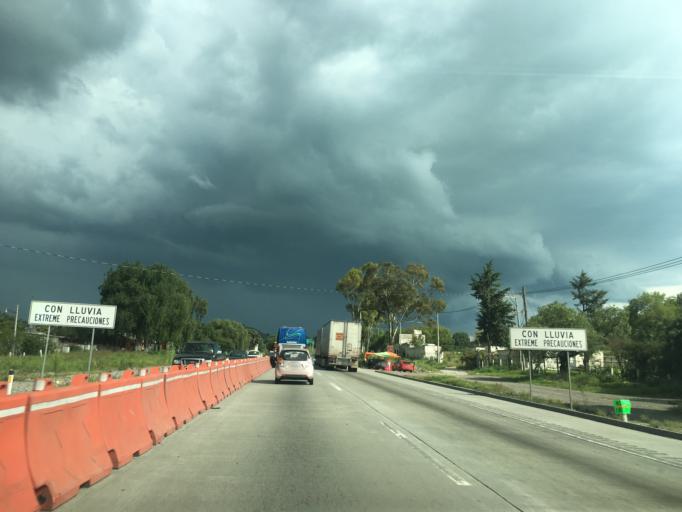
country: MX
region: Hidalgo
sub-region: Tepeji del Rio de Ocampo
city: Santiago Tlapanaloya
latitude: 19.8744
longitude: -99.3402
